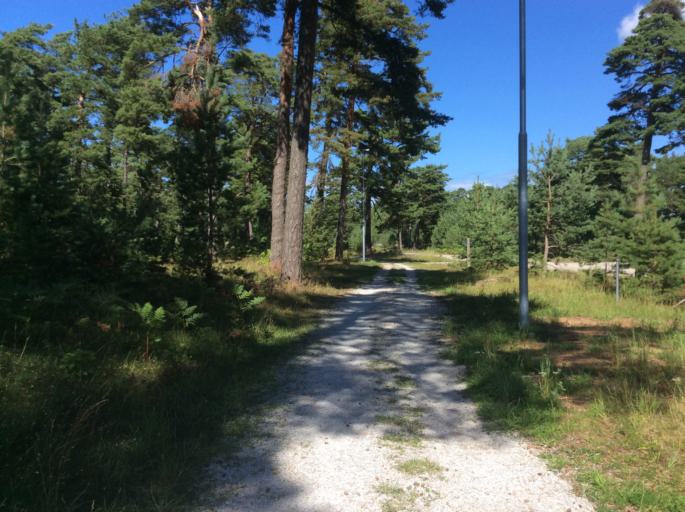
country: SE
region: Gotland
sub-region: Gotland
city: Vibble
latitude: 57.6036
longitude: 18.2811
